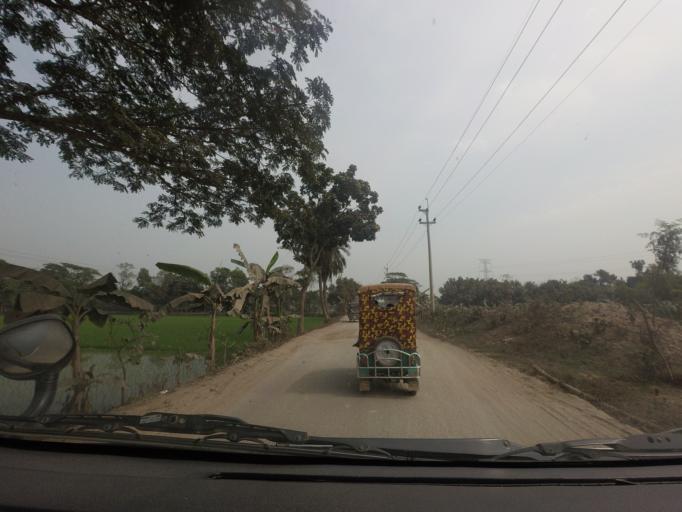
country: BD
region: Dhaka
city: Kishorganj
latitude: 24.3445
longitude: 90.7700
